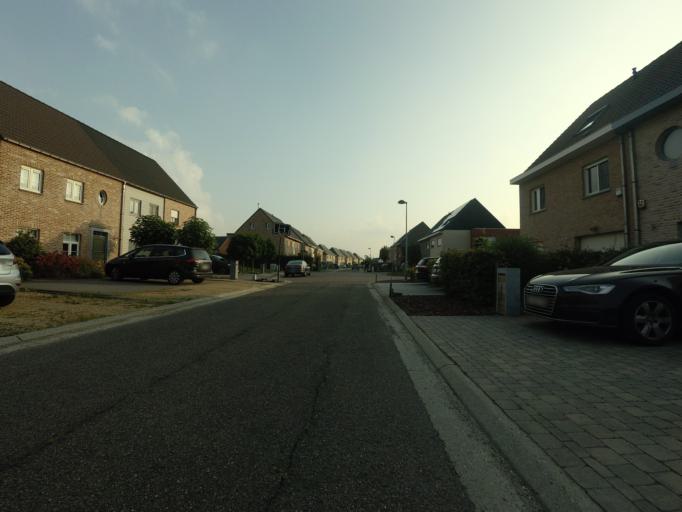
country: BE
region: Flanders
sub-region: Provincie Antwerpen
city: Willebroek
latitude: 51.0561
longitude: 4.3484
